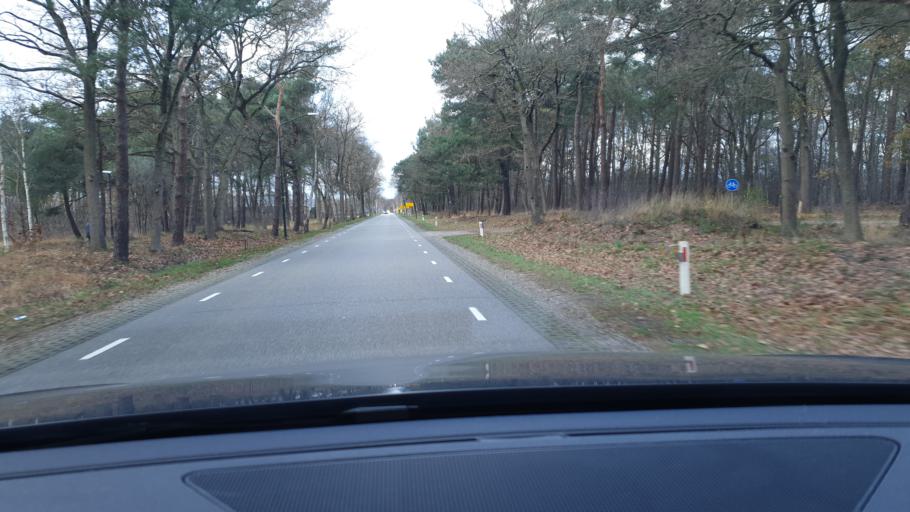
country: NL
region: North Brabant
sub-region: Gemeente Waalre
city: Waalre
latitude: 51.3864
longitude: 5.4116
